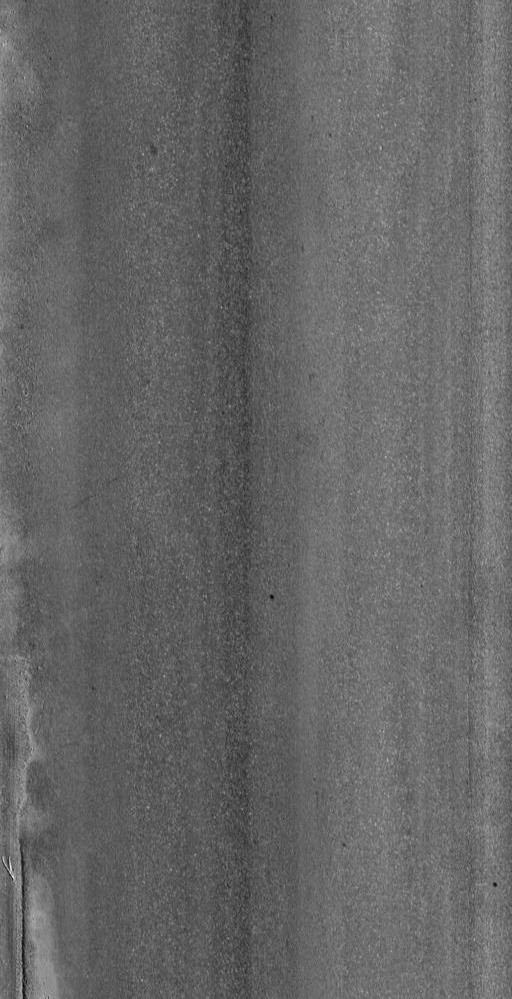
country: US
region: Vermont
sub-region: Chittenden County
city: Essex Junction
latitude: 44.4600
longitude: -73.1204
